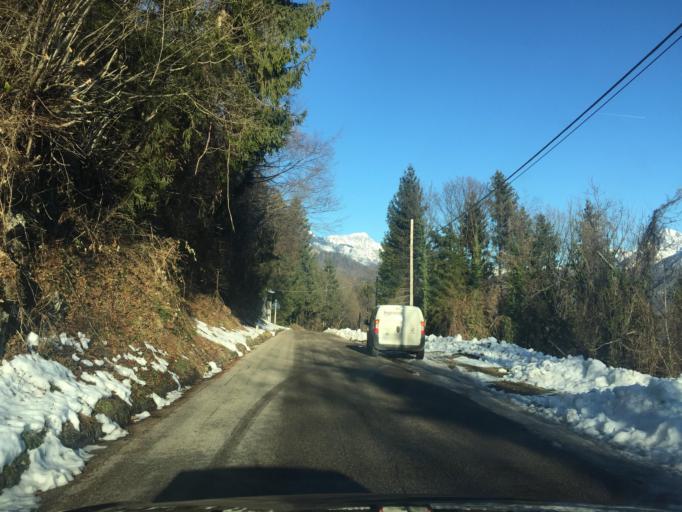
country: IT
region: Friuli Venezia Giulia
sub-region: Provincia di Udine
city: Tolmezzo
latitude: 46.4199
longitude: 12.9980
